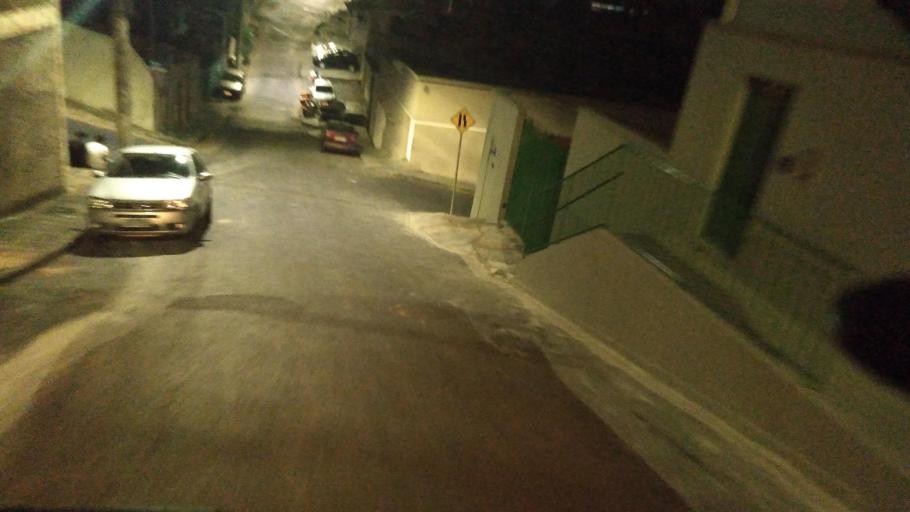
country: BR
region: Minas Gerais
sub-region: Belo Horizonte
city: Belo Horizonte
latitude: -19.8917
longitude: -43.9611
